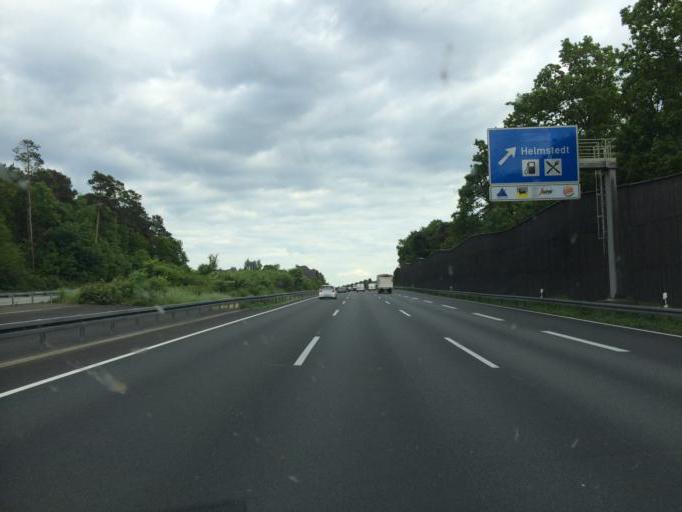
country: DE
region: Lower Saxony
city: Helmstedt
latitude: 52.2373
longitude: 11.0190
